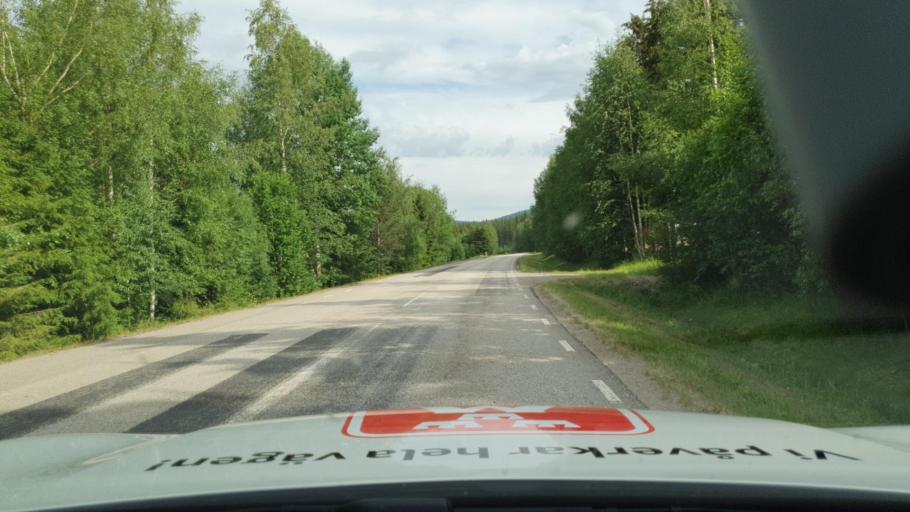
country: NO
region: Hedmark
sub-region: Trysil
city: Innbygda
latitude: 60.9157
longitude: 12.5449
